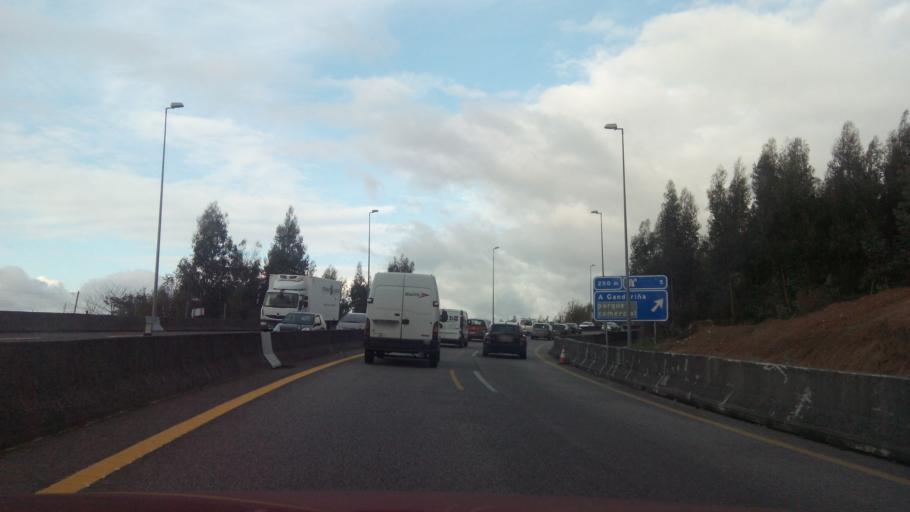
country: ES
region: Galicia
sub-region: Provincia de Pontevedra
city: Vigo
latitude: 42.2126
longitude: -8.6920
